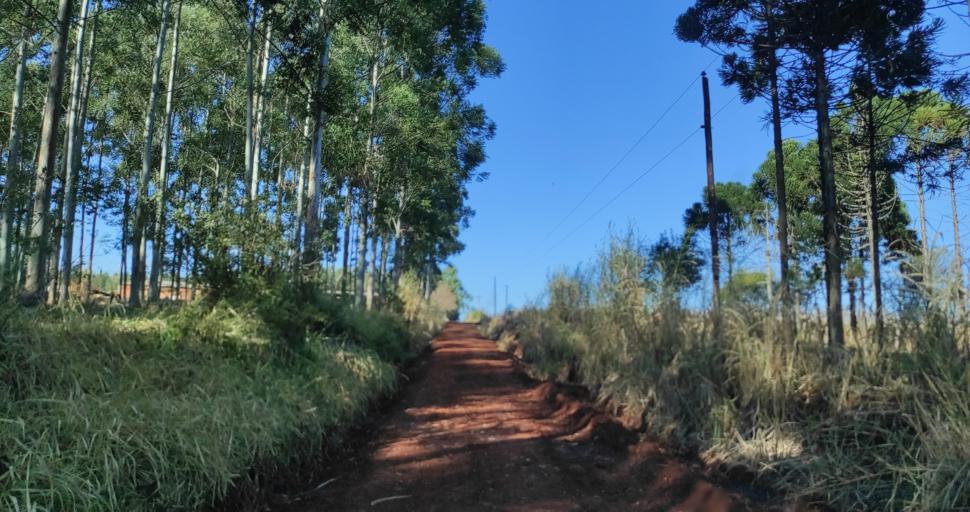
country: AR
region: Misiones
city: Capiovi
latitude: -26.8788
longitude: -55.0369
